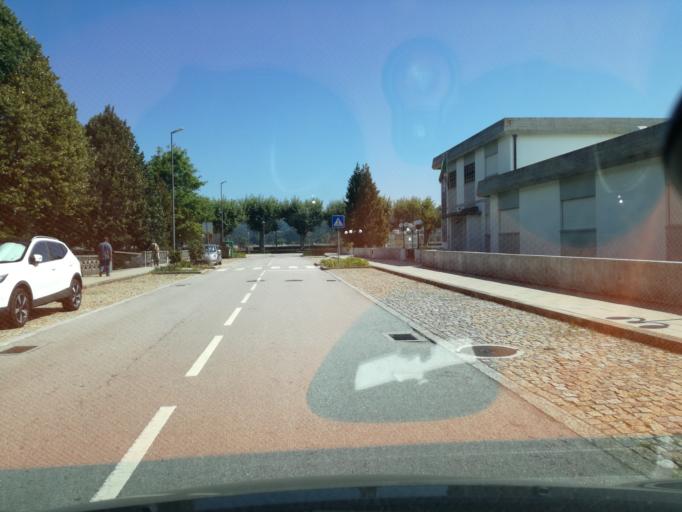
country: ES
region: Galicia
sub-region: Provincia de Pontevedra
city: A Guarda
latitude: 41.8762
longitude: -8.8350
